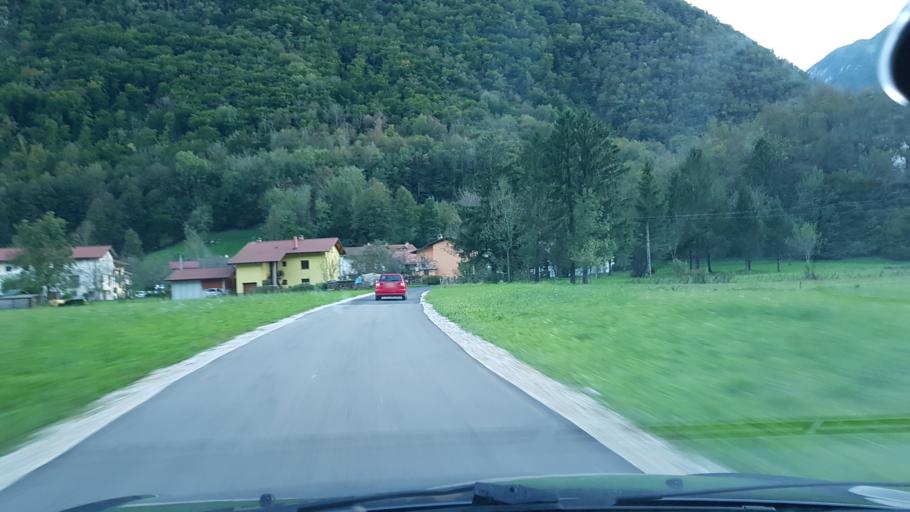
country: SI
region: Kobarid
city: Kobarid
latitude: 46.2457
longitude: 13.5152
